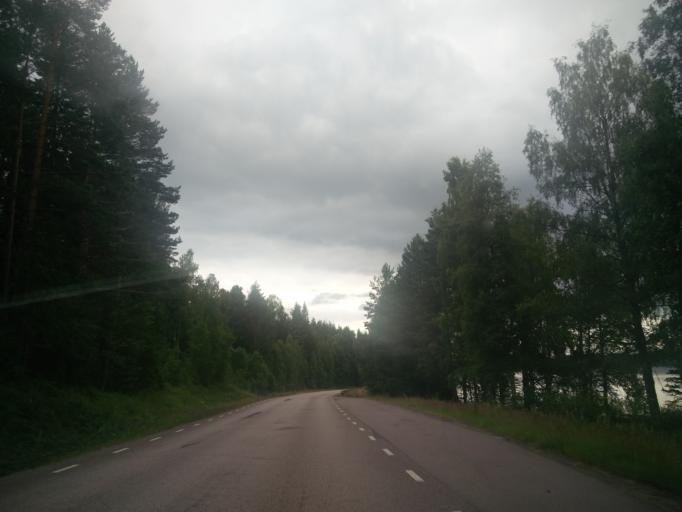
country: SE
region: Vaermland
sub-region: Arvika Kommun
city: Arvika
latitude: 59.9274
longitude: 12.6598
